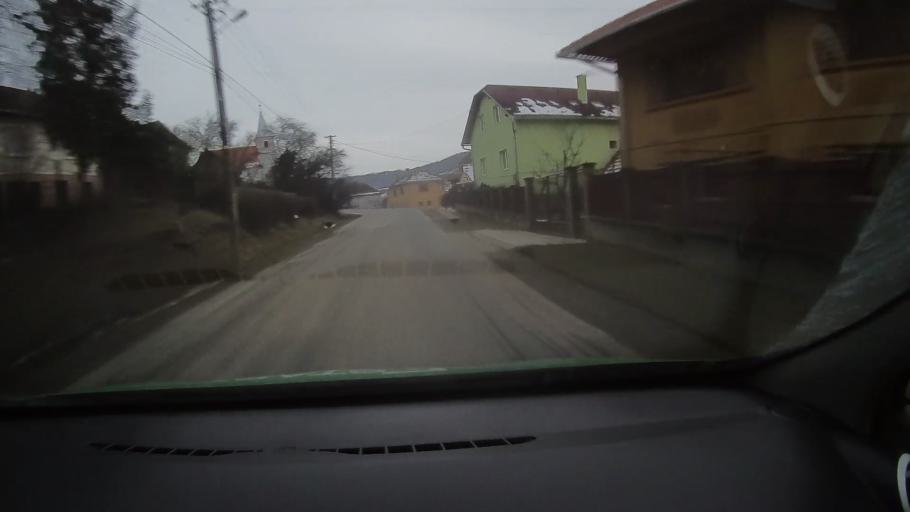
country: RO
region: Harghita
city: Taureni
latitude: 46.2581
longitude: 25.2522
